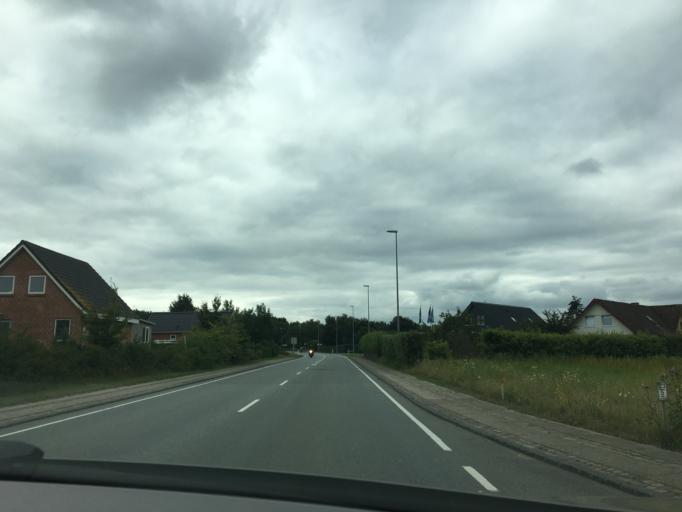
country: DK
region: Central Jutland
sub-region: Herning Kommune
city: Kibaek
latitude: 55.9389
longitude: 8.7865
